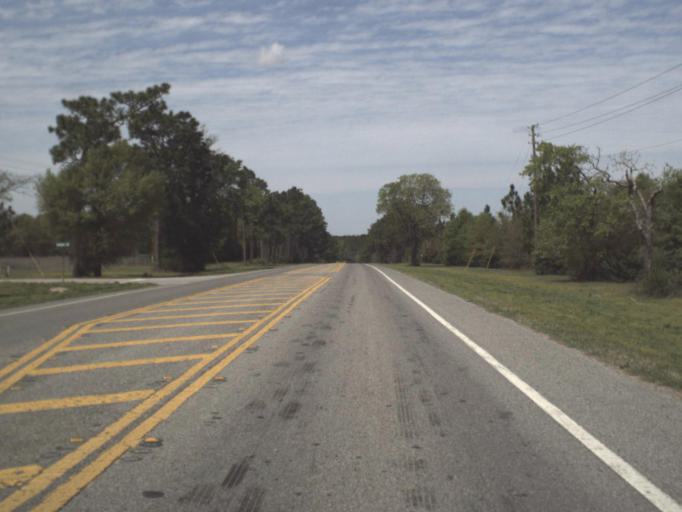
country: US
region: Florida
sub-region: Okaloosa County
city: Crestview
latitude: 30.7221
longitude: -86.6824
